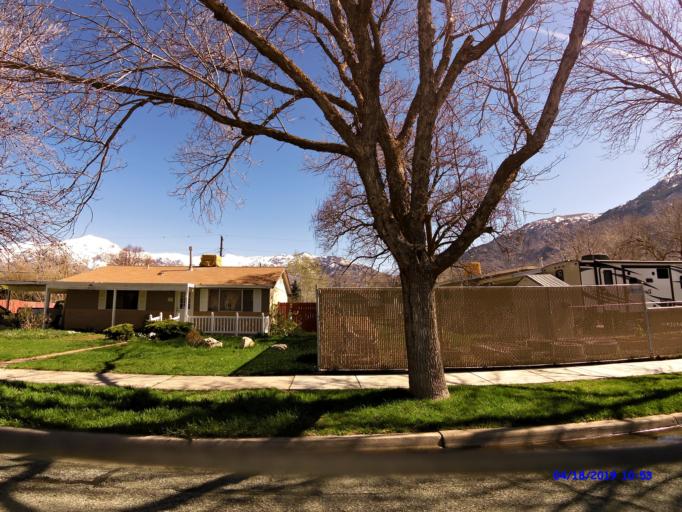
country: US
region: Utah
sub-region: Weber County
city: Harrisville
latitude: 41.2823
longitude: -111.9651
